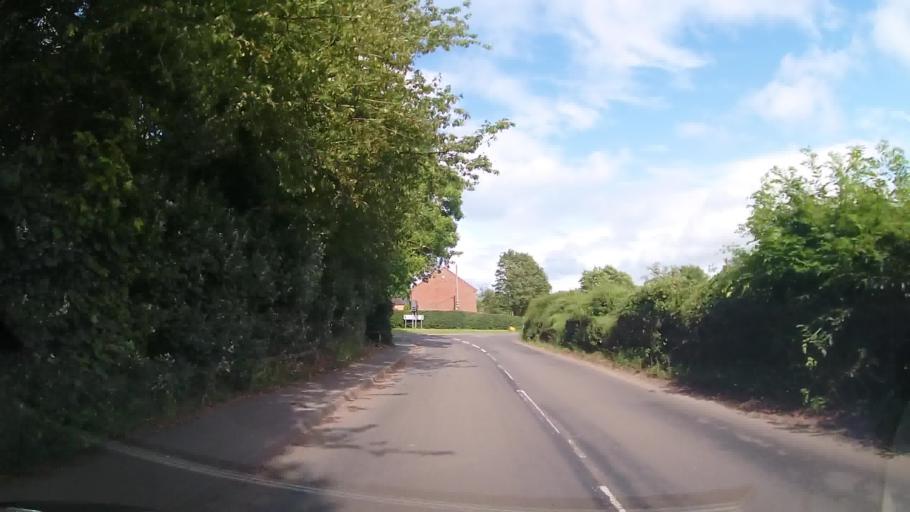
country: GB
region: England
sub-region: Shropshire
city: Petton
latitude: 52.8291
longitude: -2.8078
